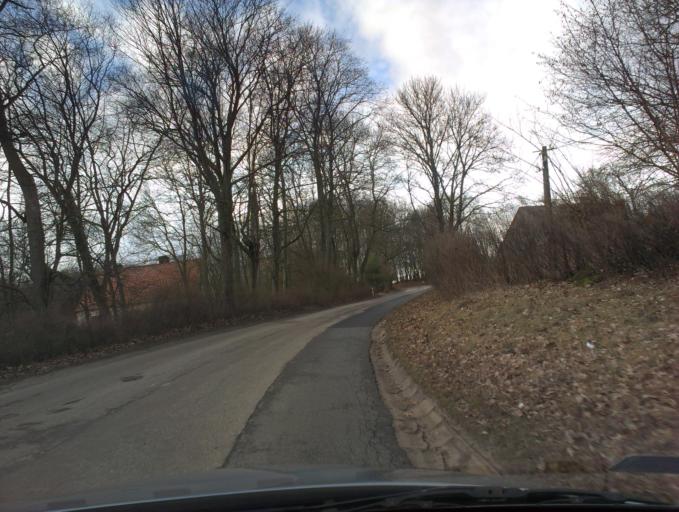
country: PL
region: Pomeranian Voivodeship
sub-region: Powiat czluchowski
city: Rzeczenica
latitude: 53.6699
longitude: 17.1020
